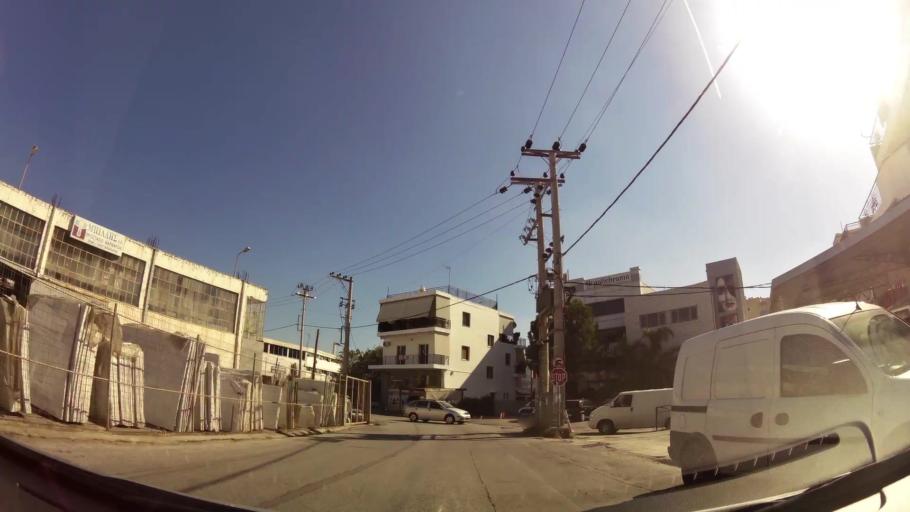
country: GR
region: Attica
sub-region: Nomarchia Athinas
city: Metamorfosi
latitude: 38.0701
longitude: 23.7684
